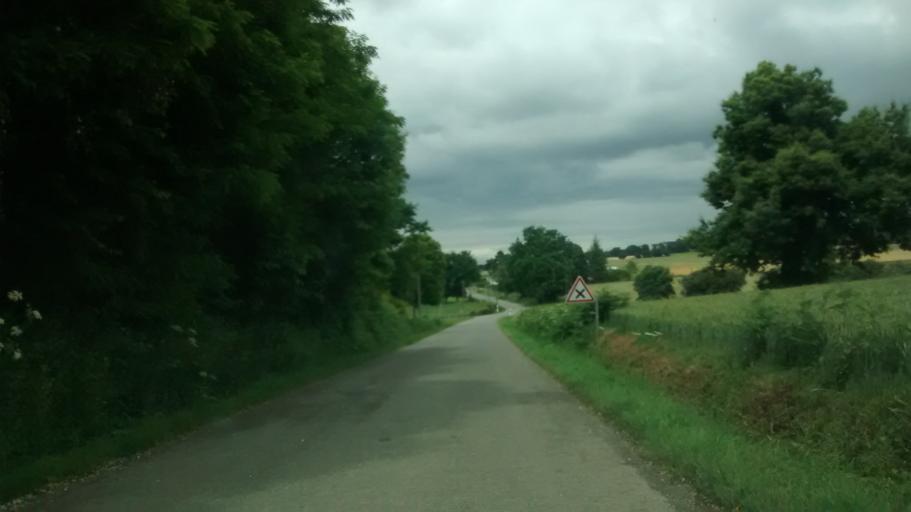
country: FR
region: Brittany
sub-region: Departement d'Ille-et-Vilaine
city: Sixt-sur-Aff
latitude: 47.7935
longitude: -2.1058
